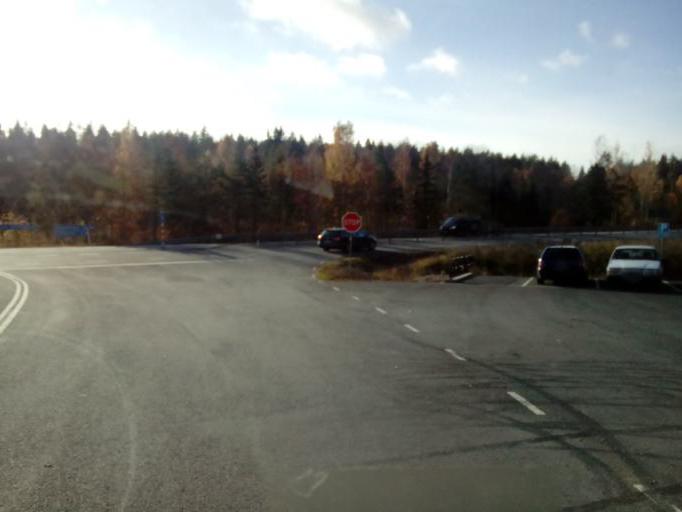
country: SE
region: Kalmar
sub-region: Vimmerby Kommun
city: Vimmerby
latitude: 57.7178
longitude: 16.0668
